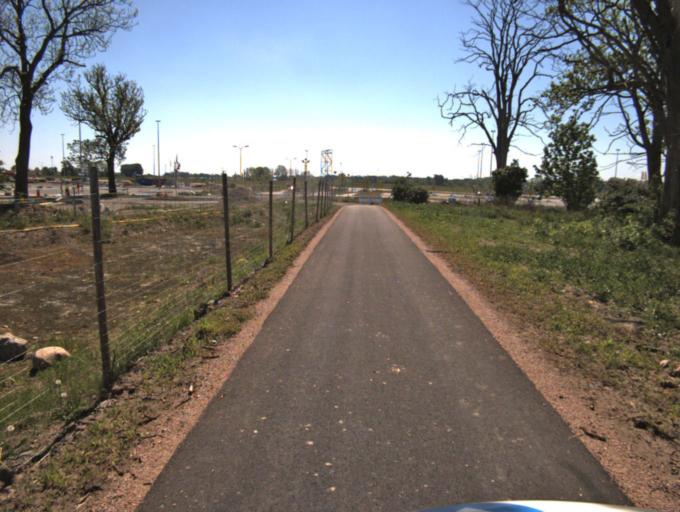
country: SE
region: Skane
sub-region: Kristianstads Kommun
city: Kristianstad
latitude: 56.0260
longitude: 14.2015
